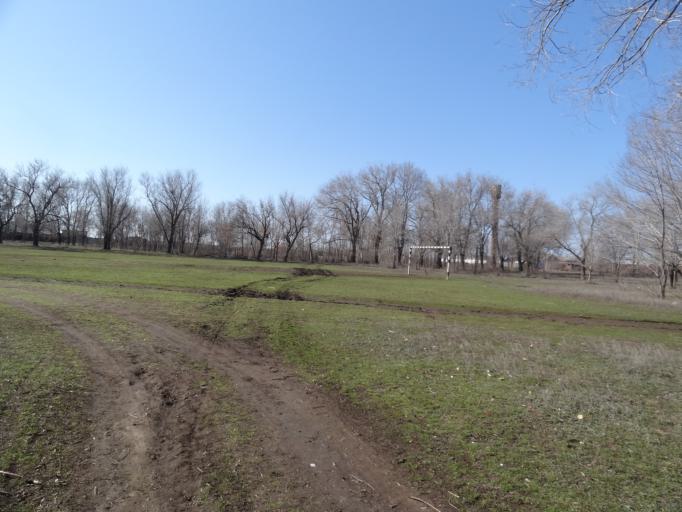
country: RU
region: Saratov
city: Shumeyka
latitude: 51.3896
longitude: 46.2977
